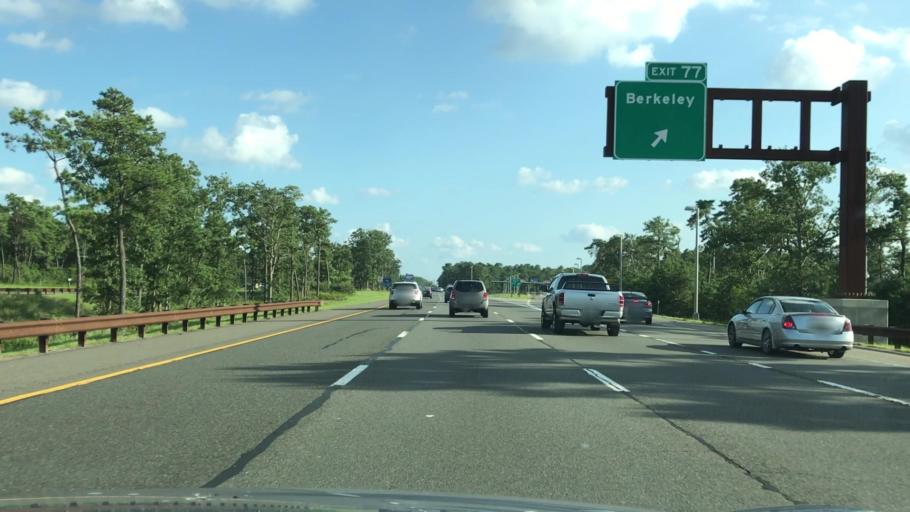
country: US
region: New Jersey
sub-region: Ocean County
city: South Toms River
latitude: 39.9093
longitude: -74.2125
